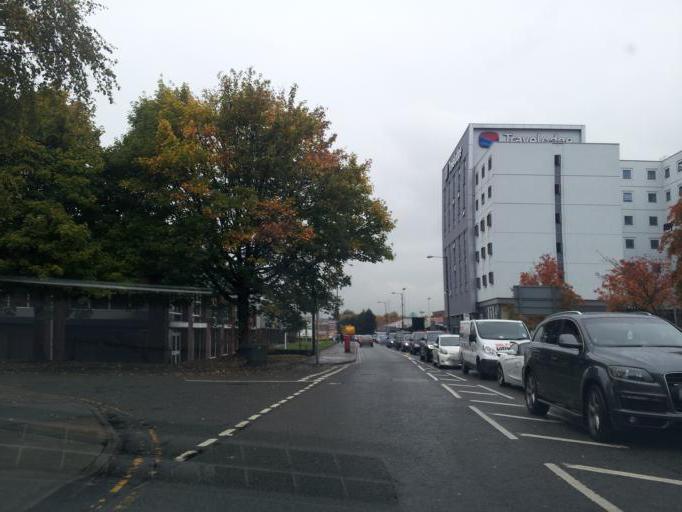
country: GB
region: England
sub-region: Manchester
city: Cheetham Hill
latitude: 53.4894
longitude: -2.2465
